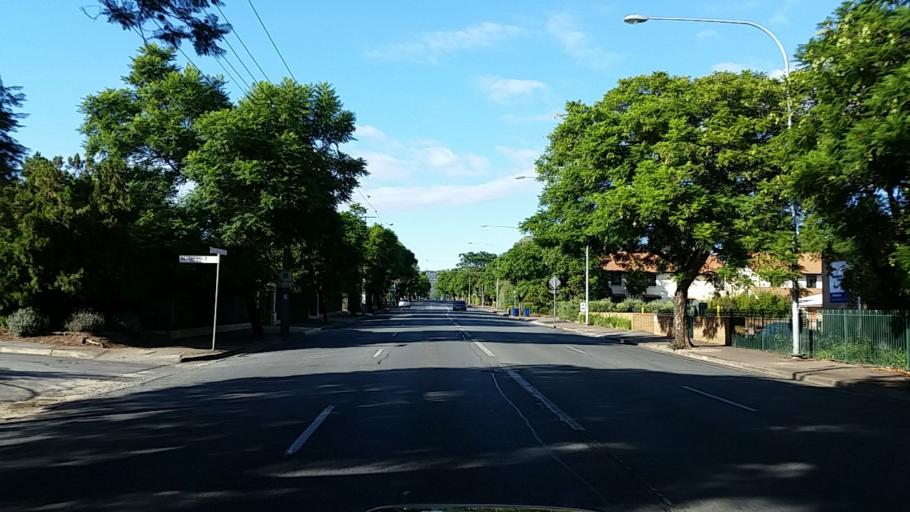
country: AU
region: South Australia
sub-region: Unley
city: Fullarton
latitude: -34.9524
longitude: 138.6255
